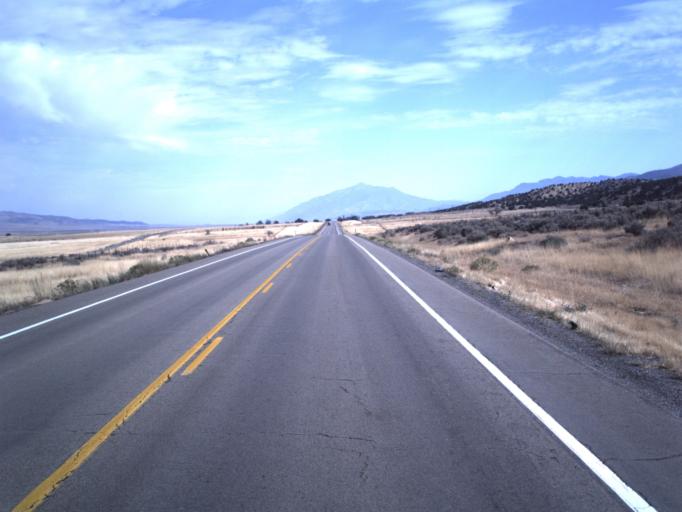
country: US
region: Utah
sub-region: Sanpete County
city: Gunnison
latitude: 39.4166
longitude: -111.9234
